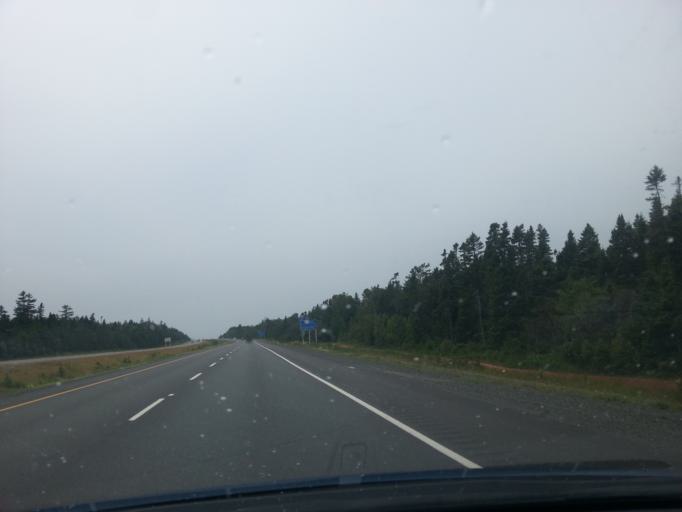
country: CA
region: Nova Scotia
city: Truro
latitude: 45.3978
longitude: -63.4617
